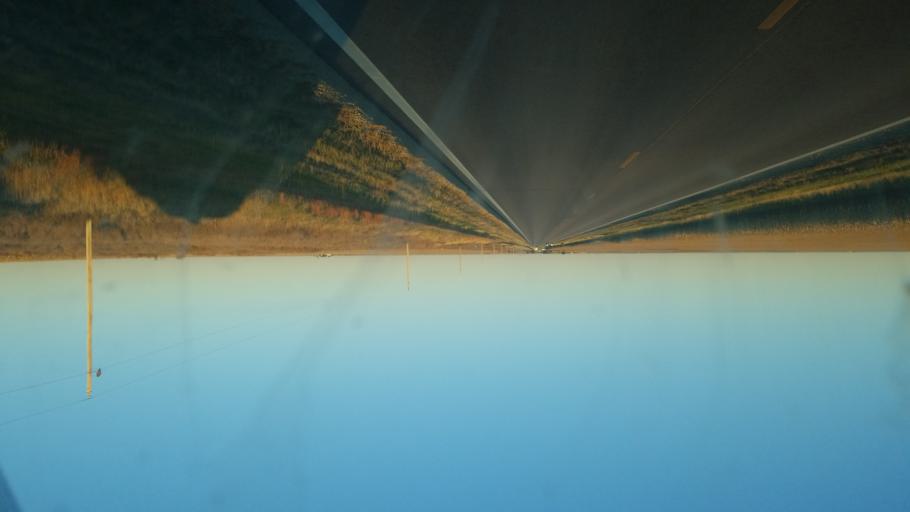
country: US
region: Kansas
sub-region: Wallace County
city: Sharon Springs
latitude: 38.8610
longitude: -102.0212
